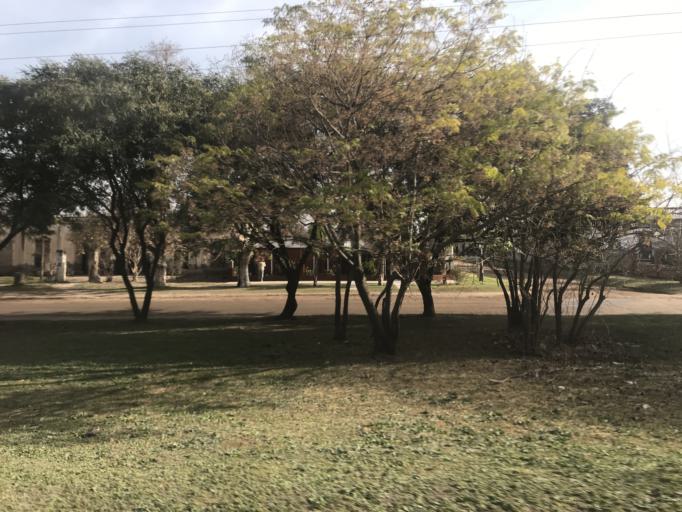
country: AR
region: Cordoba
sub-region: Departamento de Rio Segundo
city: Rio Segundo
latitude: -31.6576
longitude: -63.9070
